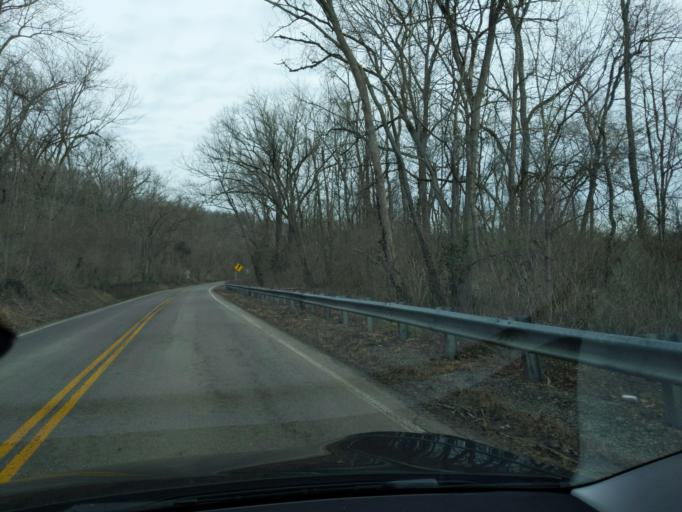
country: US
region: Kentucky
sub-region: Clark County
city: Winchester
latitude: 37.8980
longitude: -84.2688
